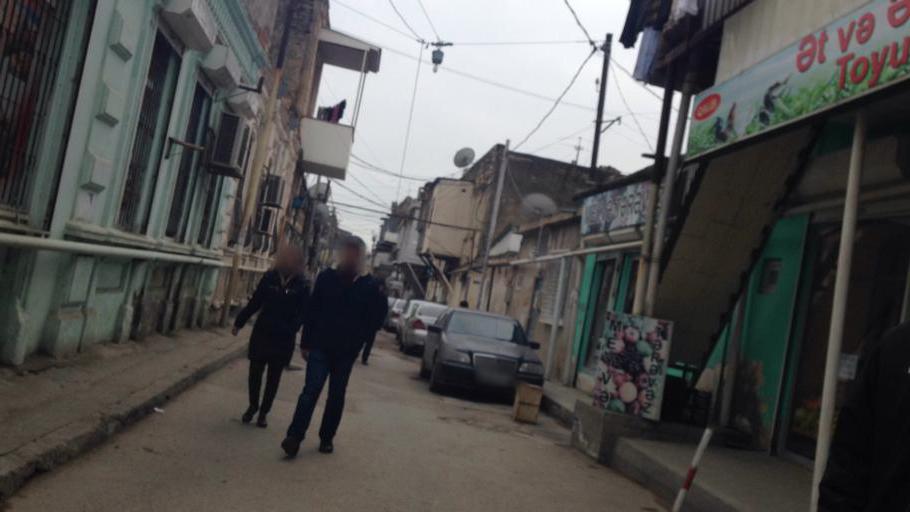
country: AZ
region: Baki
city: Badamdar
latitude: 40.3786
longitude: 49.8292
